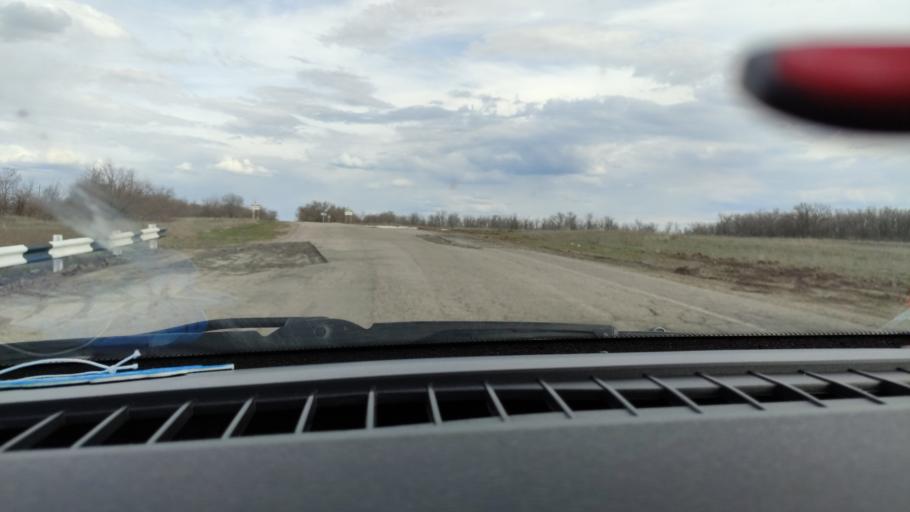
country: RU
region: Saratov
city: Rovnoye
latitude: 51.0444
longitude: 46.0591
